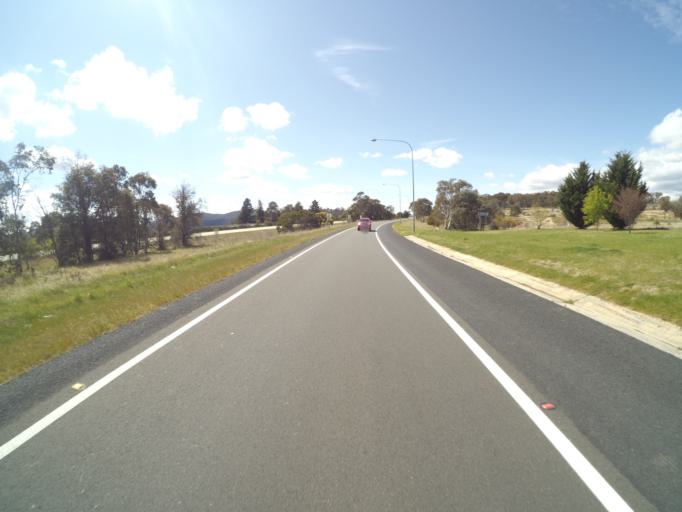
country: AU
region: New South Wales
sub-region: Goulburn Mulwaree
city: Goulburn
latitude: -34.7409
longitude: 149.7756
